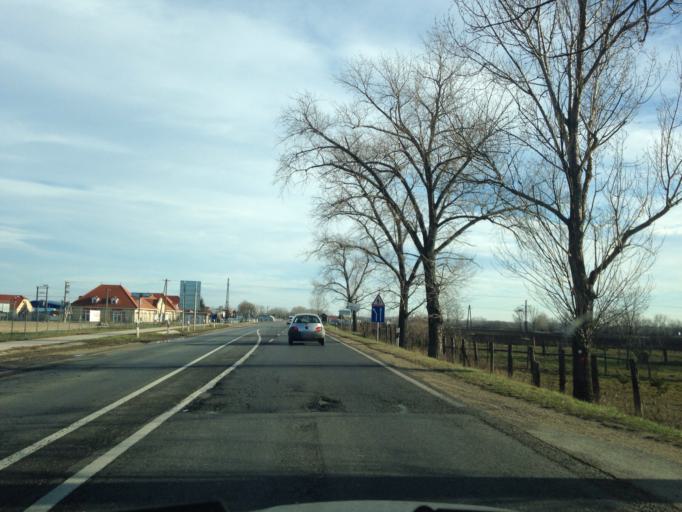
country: HU
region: Gyor-Moson-Sopron
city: Abda
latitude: 47.6801
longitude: 17.5796
